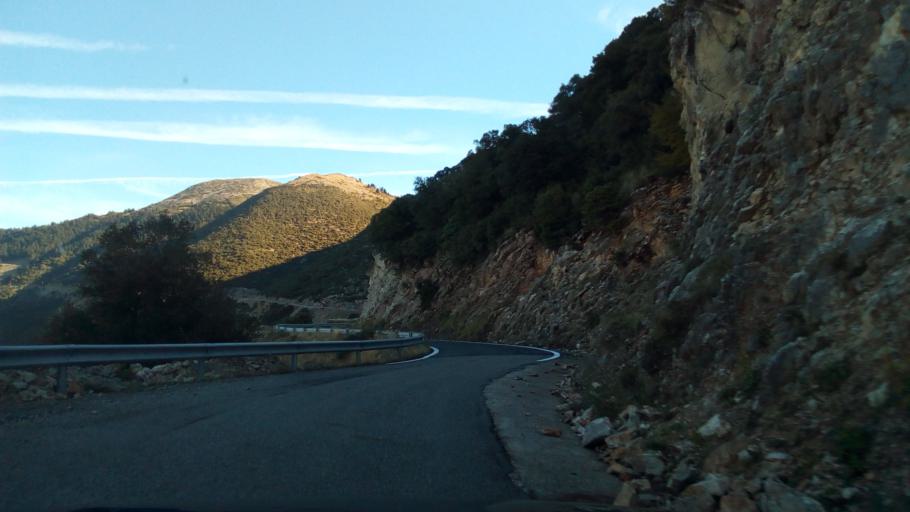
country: GR
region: West Greece
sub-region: Nomos Aitolias kai Akarnanias
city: Nafpaktos
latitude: 38.5105
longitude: 21.8428
